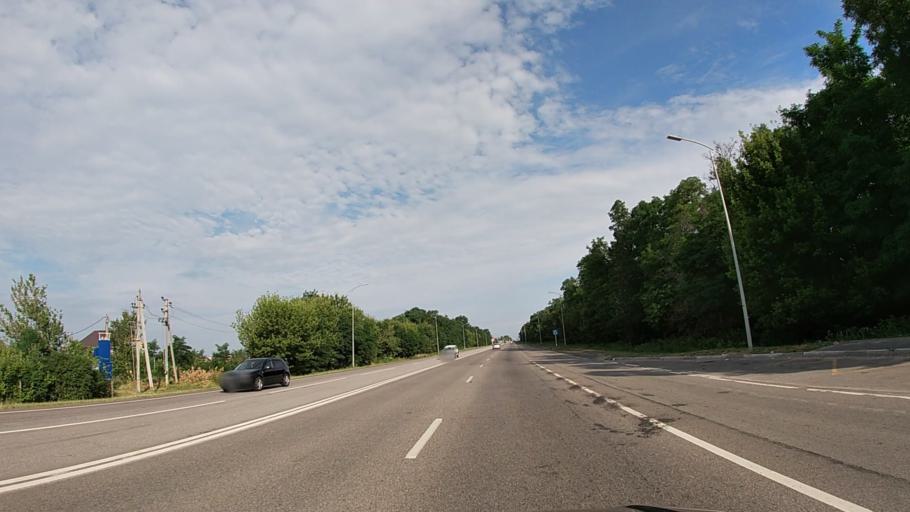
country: RU
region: Belgorod
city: Severnyy
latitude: 50.6389
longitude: 36.4421
